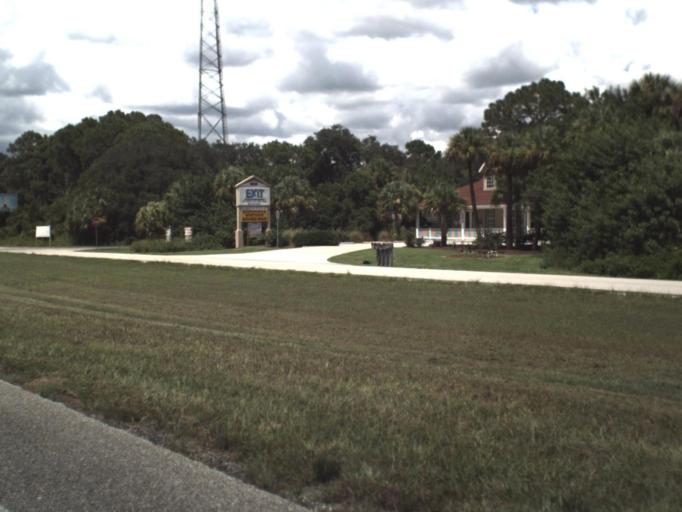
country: US
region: Florida
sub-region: Sarasota County
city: North Port
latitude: 27.0223
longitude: -82.1898
